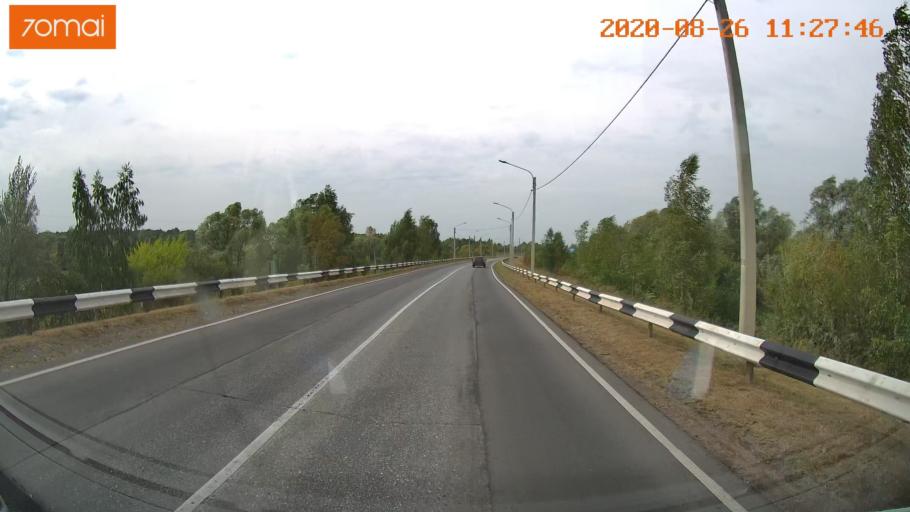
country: RU
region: Rjazan
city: Shilovo
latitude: 54.3247
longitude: 40.9292
